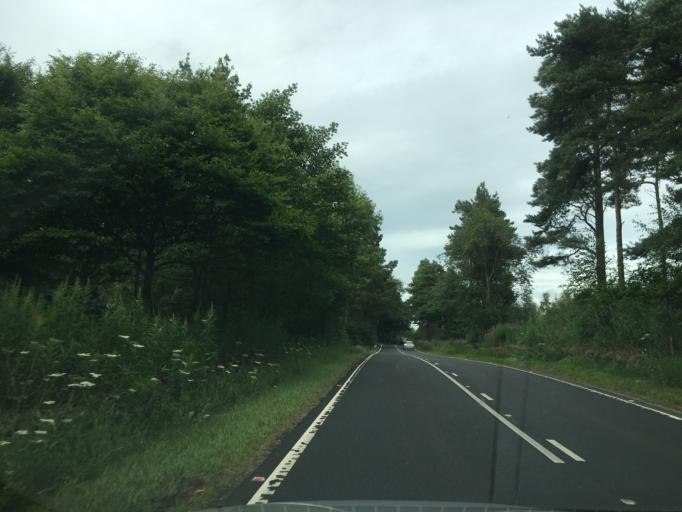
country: GB
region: Scotland
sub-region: South Lanarkshire
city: Biggar
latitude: 55.5765
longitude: -3.5805
